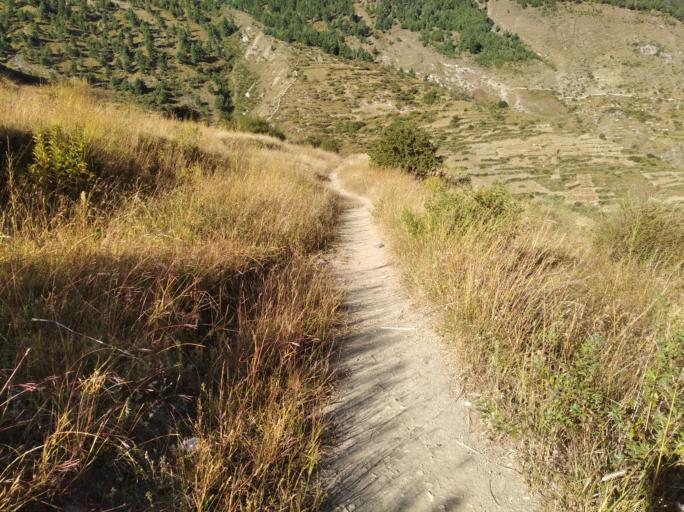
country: NP
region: Western Region
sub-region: Dhawalagiri Zone
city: Jomsom
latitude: 28.8813
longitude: 82.9751
